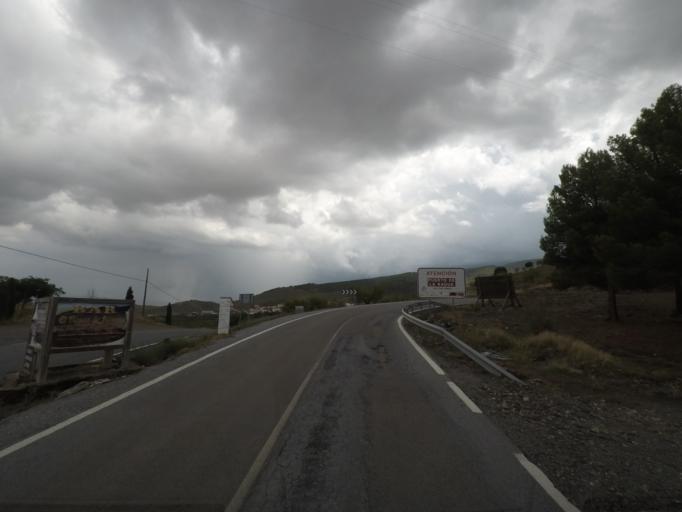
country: ES
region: Andalusia
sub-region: Provincia de Granada
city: Ferreira
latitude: 37.1750
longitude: -3.0477
